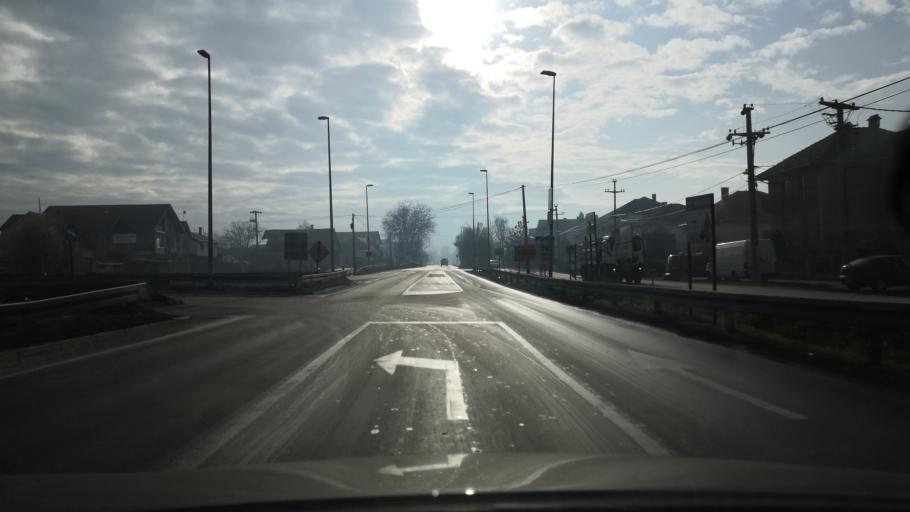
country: RS
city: Dobanovci
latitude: 44.8419
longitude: 20.2129
